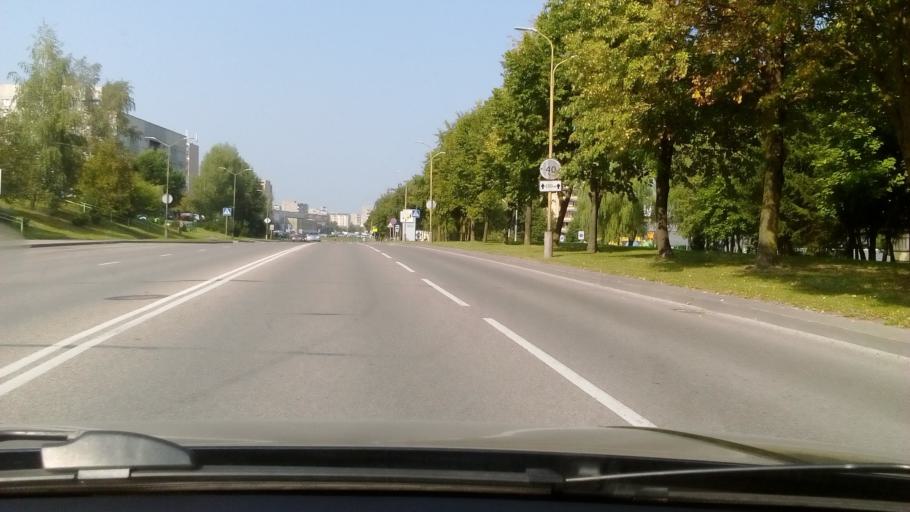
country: LT
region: Alytaus apskritis
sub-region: Alytus
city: Alytus
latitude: 54.3902
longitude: 24.0226
